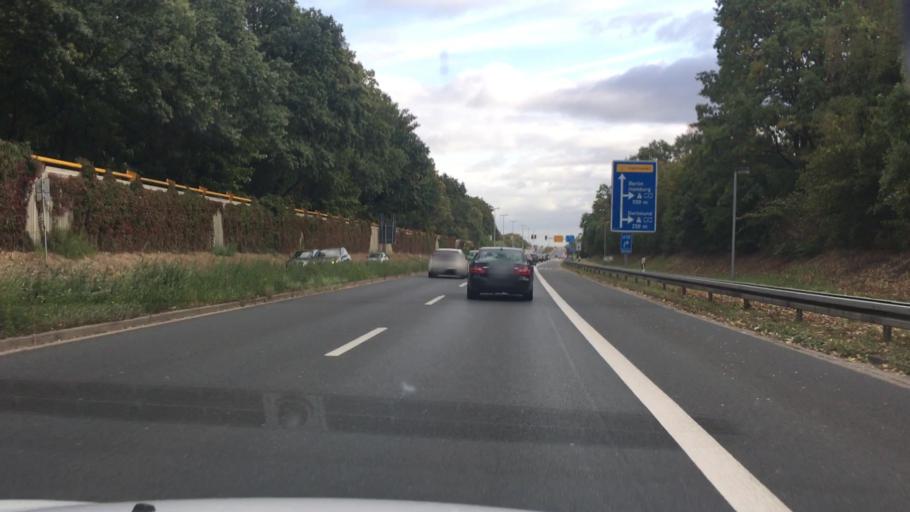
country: DE
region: Lower Saxony
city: Garbsen-Mitte
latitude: 52.4250
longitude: 9.6243
